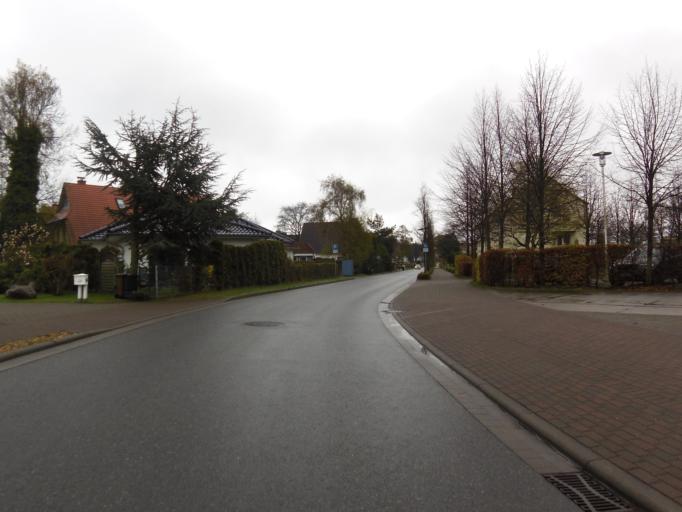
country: DE
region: Mecklenburg-Vorpommern
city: Zingst
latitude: 54.4393
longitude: 12.7014
